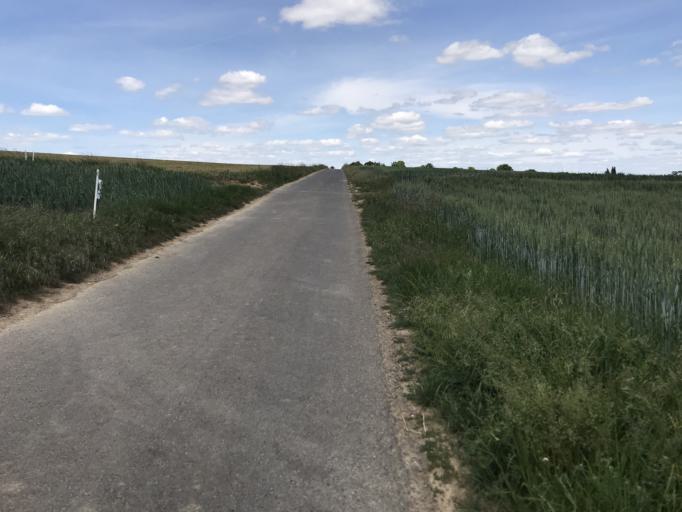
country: DE
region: Hesse
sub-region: Regierungsbezirk Darmstadt
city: Butzbach
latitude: 50.4501
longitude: 8.6523
